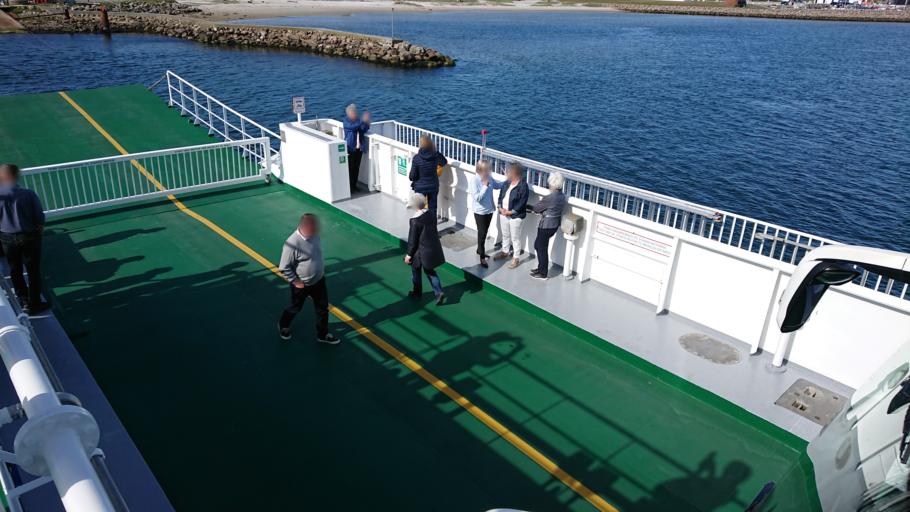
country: DK
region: Central Jutland
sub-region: Norddjurs Kommune
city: Allingabro
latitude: 56.6087
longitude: 10.3007
